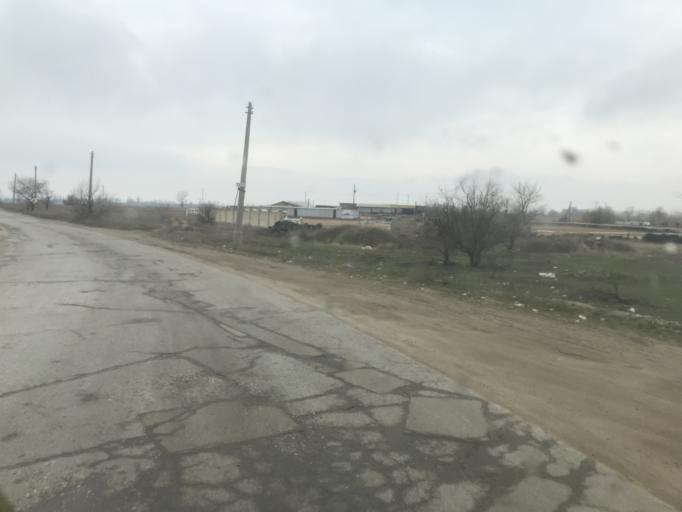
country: RU
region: Volgograd
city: Krasnoslobodsk
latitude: 48.5366
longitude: 44.6072
